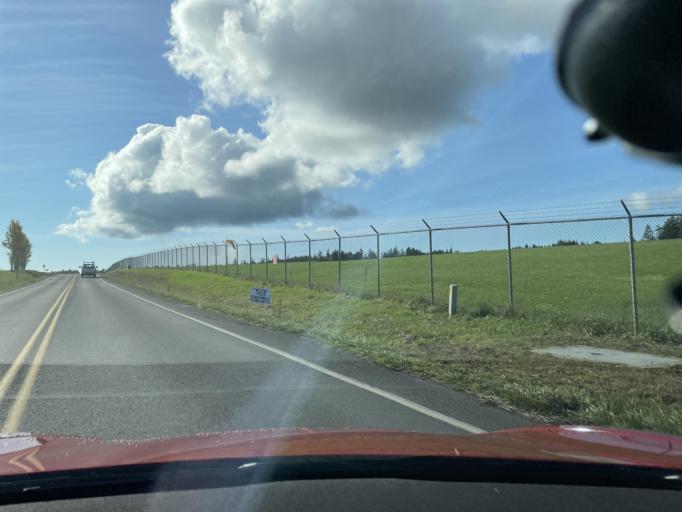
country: US
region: Washington
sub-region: San Juan County
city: Friday Harbor
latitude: 48.5217
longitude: -123.0231
